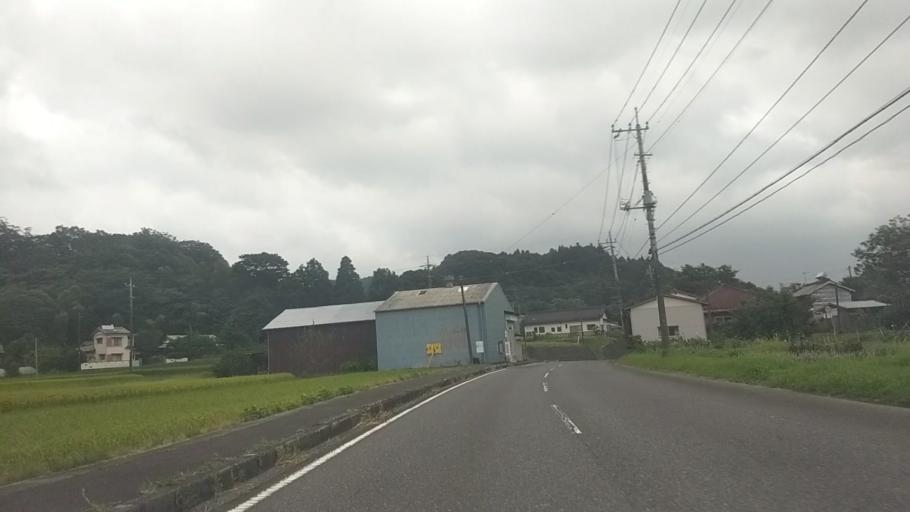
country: JP
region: Chiba
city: Kawaguchi
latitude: 35.2446
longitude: 140.0817
